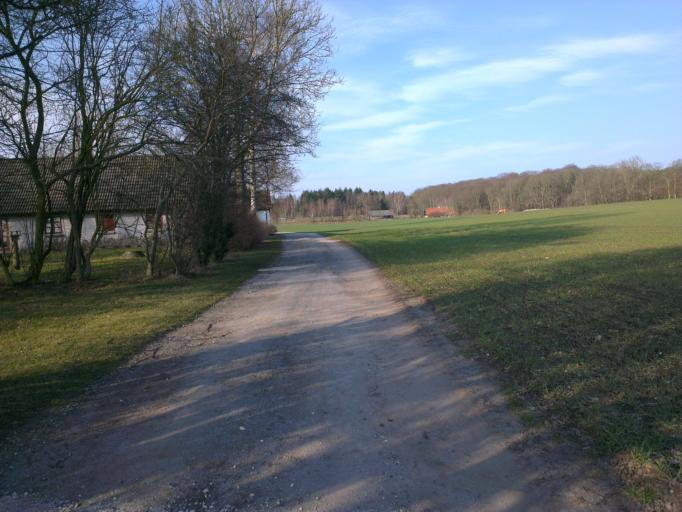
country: DK
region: Capital Region
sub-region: Frederikssund Kommune
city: Jaegerspris
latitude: 55.8456
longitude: 12.0102
